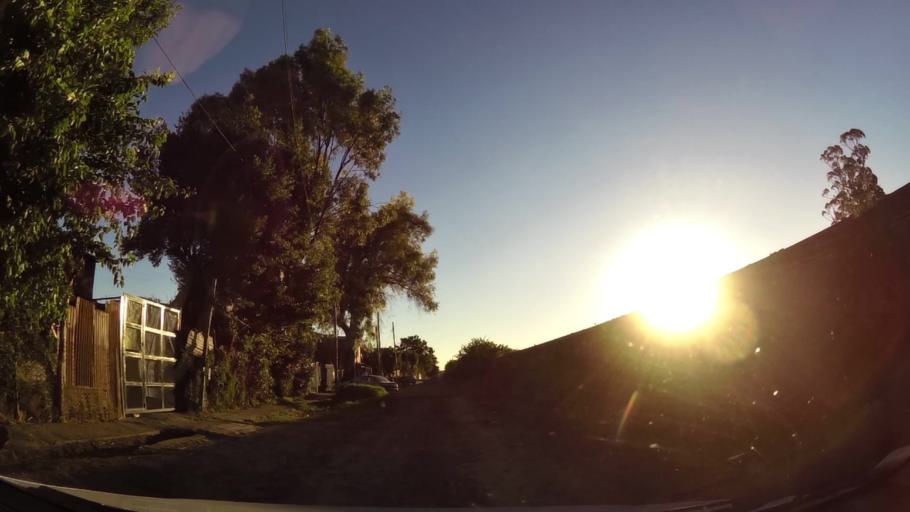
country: AR
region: Buenos Aires
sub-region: Partido de Moron
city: Moron
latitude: -34.7253
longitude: -58.6140
